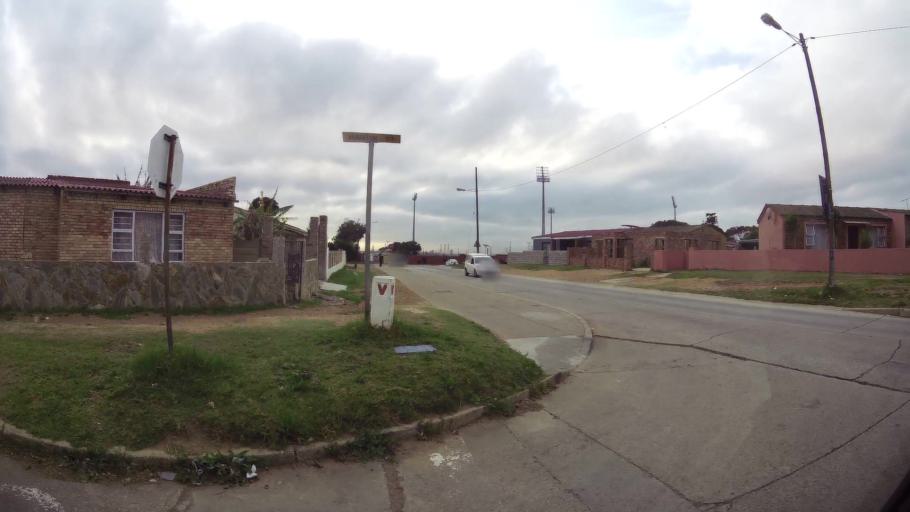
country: ZA
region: Eastern Cape
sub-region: Nelson Mandela Bay Metropolitan Municipality
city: Port Elizabeth
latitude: -33.9141
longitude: 25.5573
